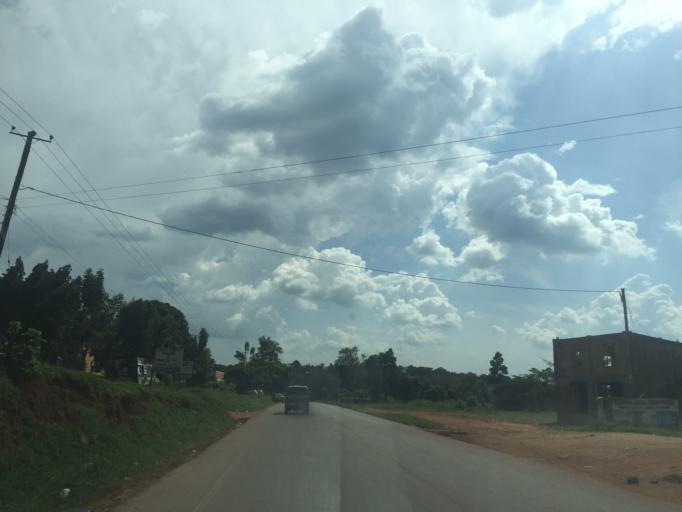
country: UG
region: Central Region
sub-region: Luwero District
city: Wobulenzi
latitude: 0.7029
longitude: 32.5246
